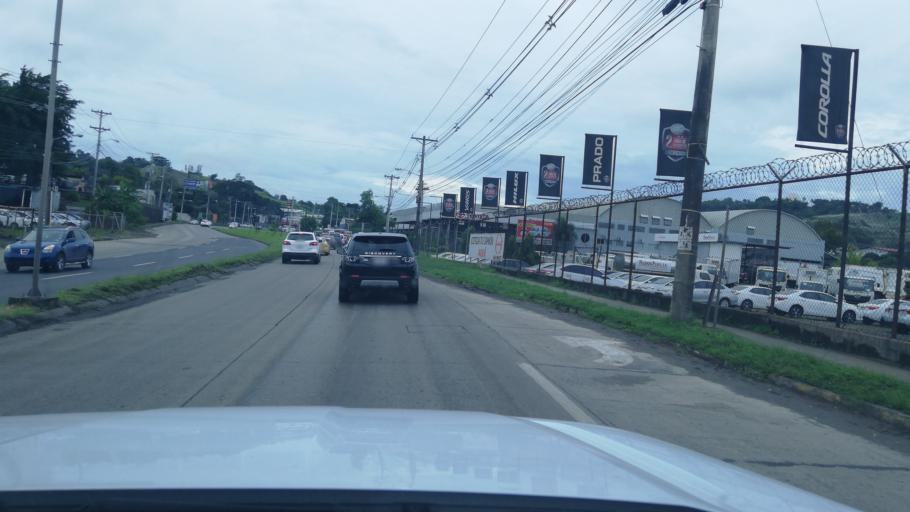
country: PA
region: Panama
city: Las Cumbres
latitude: 9.0717
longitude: -79.5227
